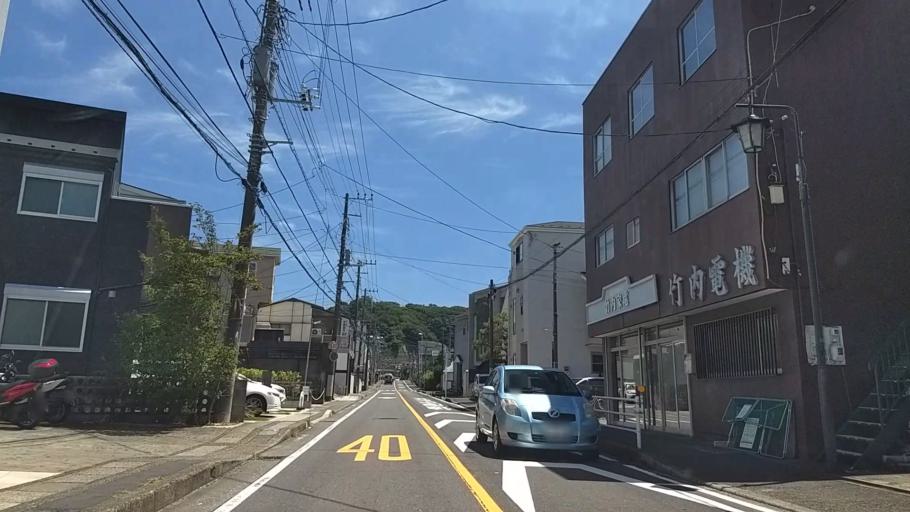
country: JP
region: Kanagawa
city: Kamakura
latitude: 35.3125
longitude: 139.5568
